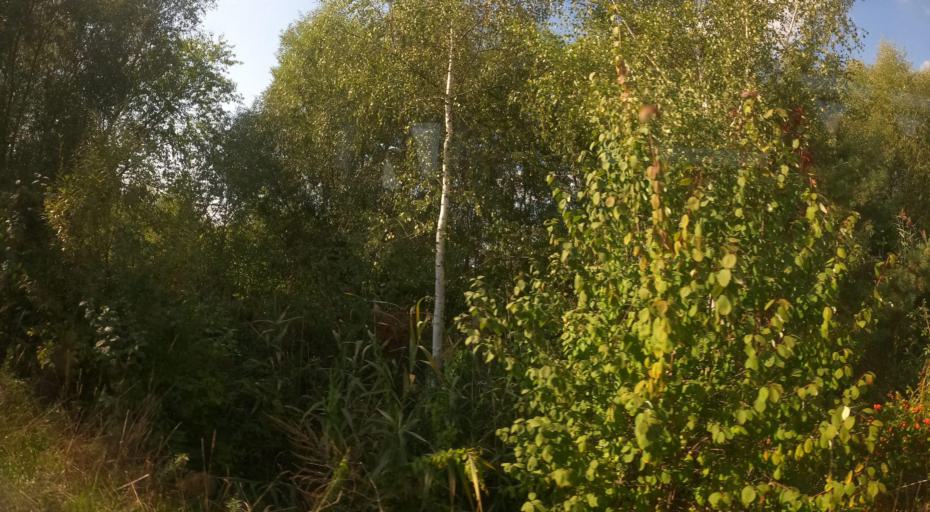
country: PL
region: Lubusz
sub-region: Powiat zielonogorski
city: Swidnica
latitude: 51.8739
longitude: 15.3200
